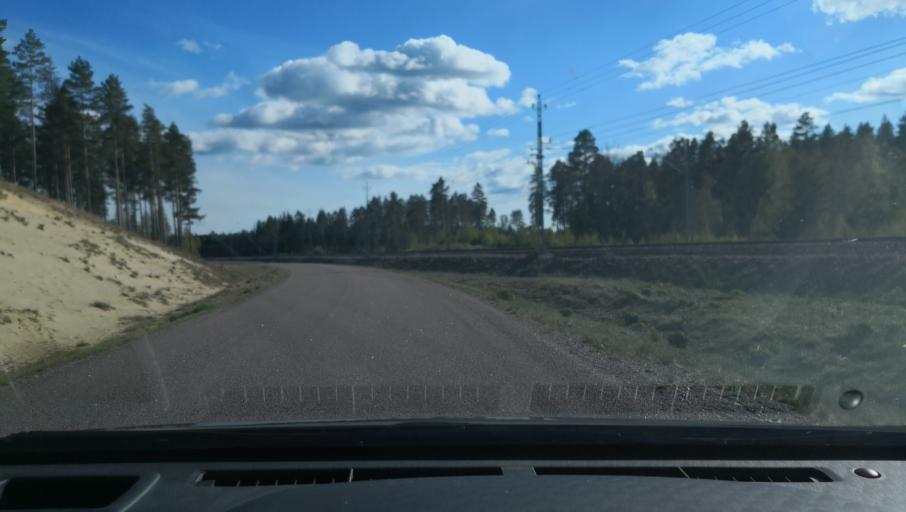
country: SE
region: OErebro
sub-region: Askersunds Kommun
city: Asbro
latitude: 58.9452
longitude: 15.0411
